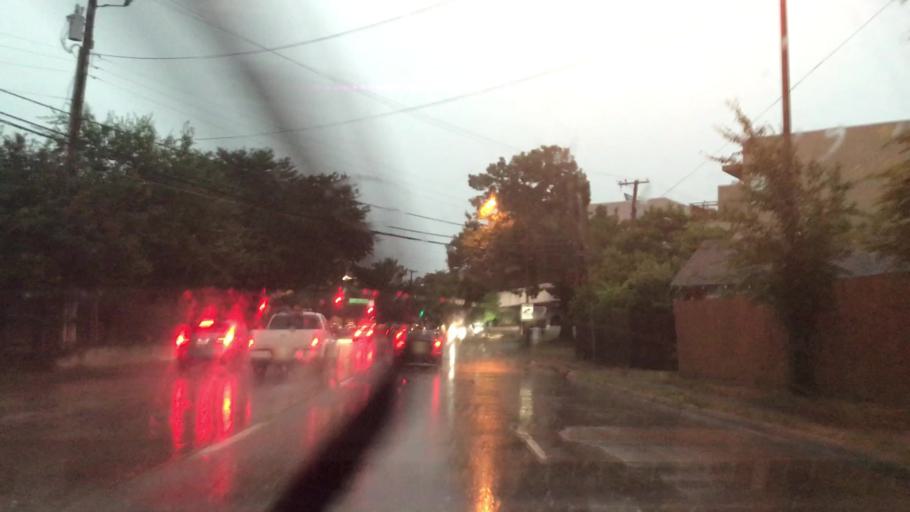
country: US
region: Texas
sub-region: Dallas County
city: Highland Park
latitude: 32.8131
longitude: -96.8150
